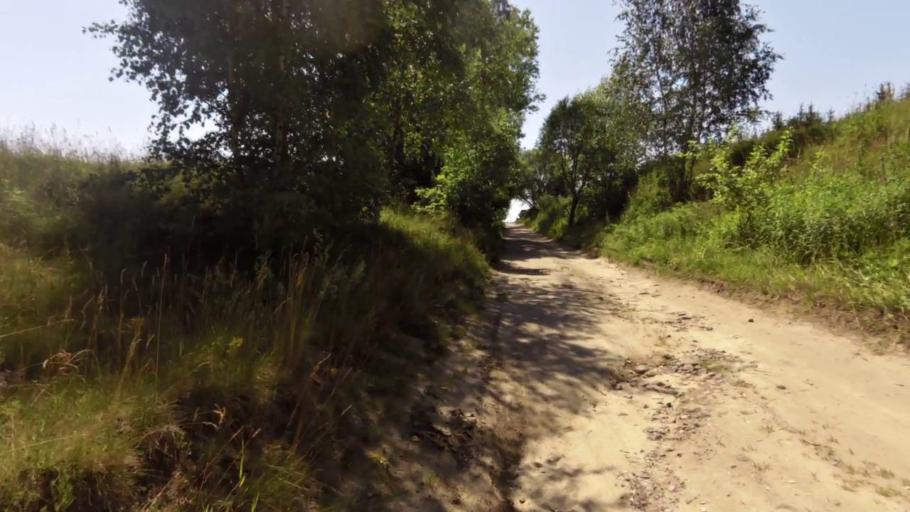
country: PL
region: West Pomeranian Voivodeship
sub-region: Powiat swidwinski
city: Polczyn-Zdroj
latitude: 53.7824
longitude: 16.1103
